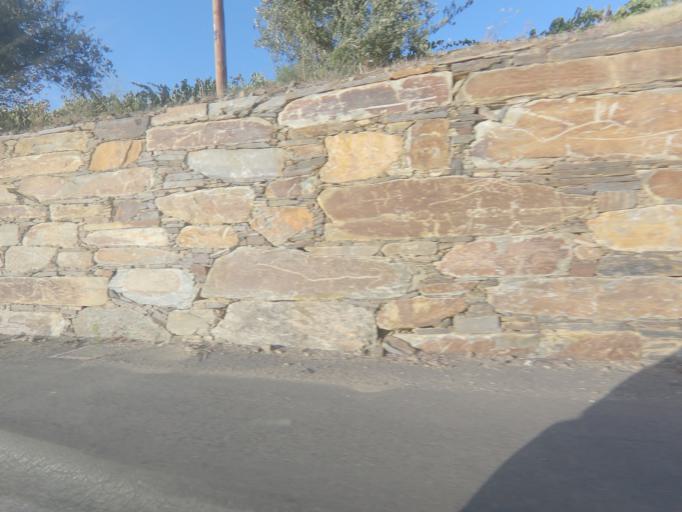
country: PT
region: Viseu
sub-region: Armamar
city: Armamar
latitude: 41.1481
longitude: -7.6782
